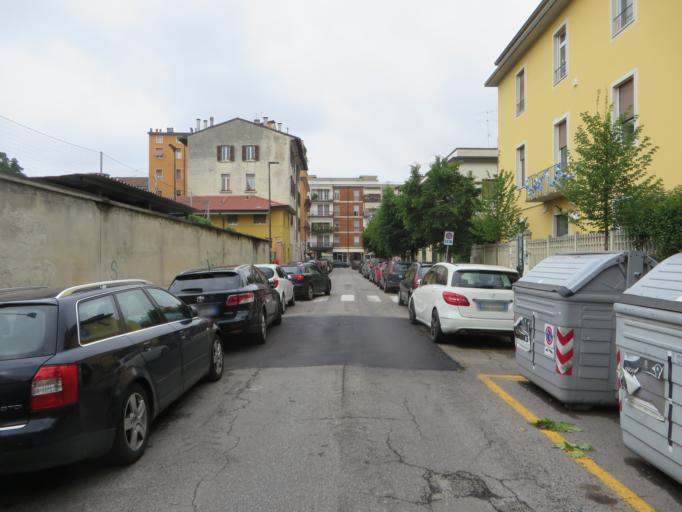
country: IT
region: Lombardy
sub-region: Provincia di Brescia
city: Brescia
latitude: 45.5265
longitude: 10.2248
